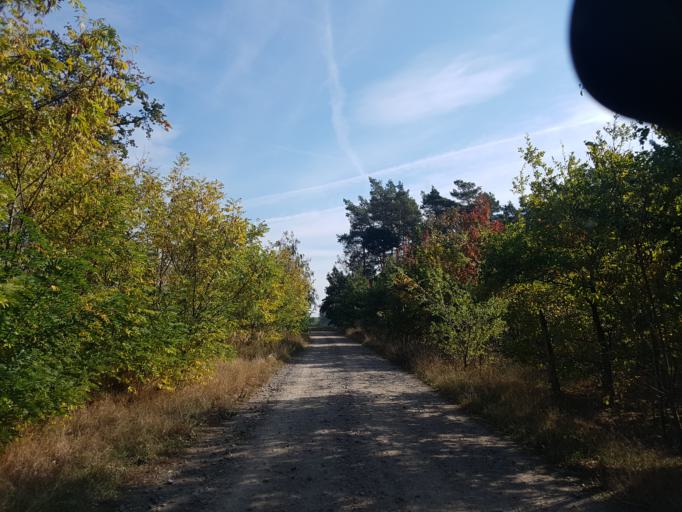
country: DE
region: Brandenburg
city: Hohenbucko
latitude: 51.7573
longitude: 13.4787
